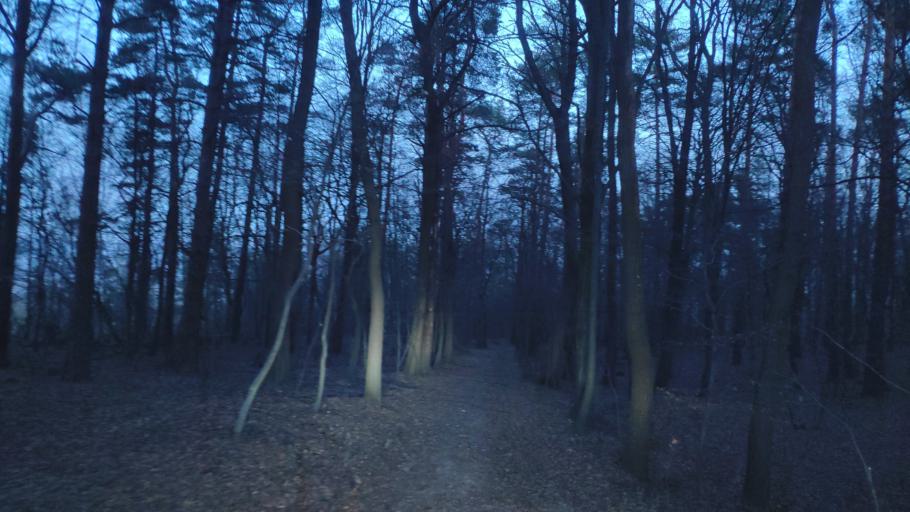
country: SK
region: Kosicky
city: Kosice
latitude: 48.8335
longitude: 21.2510
